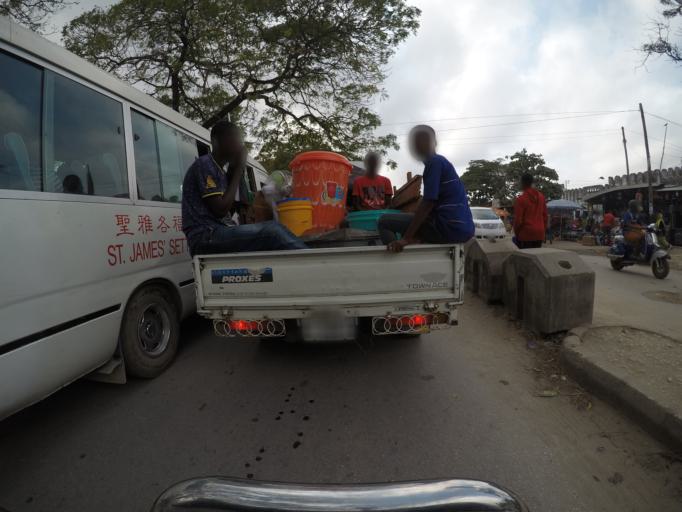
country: TZ
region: Zanzibar Urban/West
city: Zanzibar
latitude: -6.1771
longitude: 39.2248
